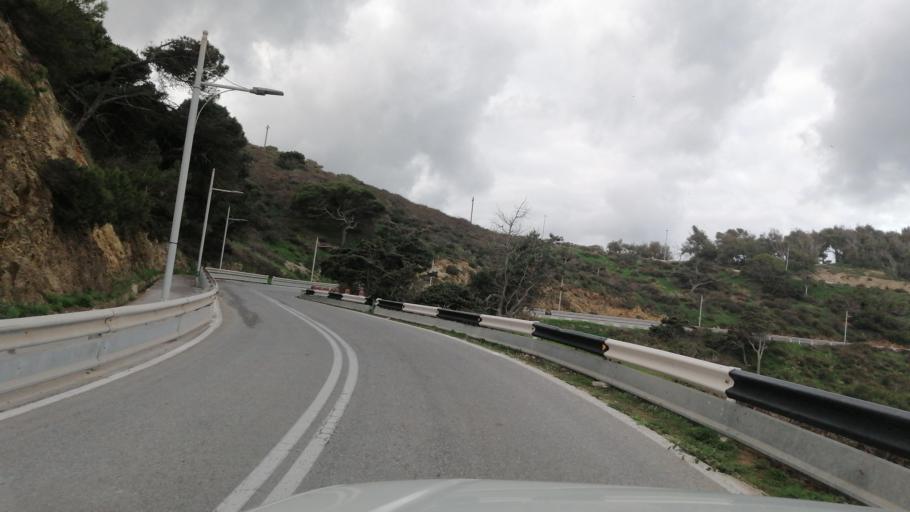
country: ES
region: Ceuta
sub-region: Ceuta
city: Ceuta
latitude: 35.8975
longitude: -5.2854
